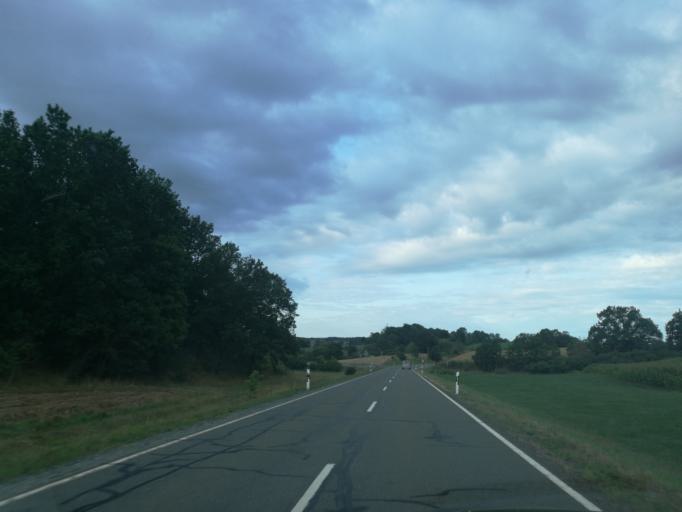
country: DE
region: Bavaria
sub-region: Upper Franconia
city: Gattendorf
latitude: 50.2990
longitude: 12.0121
